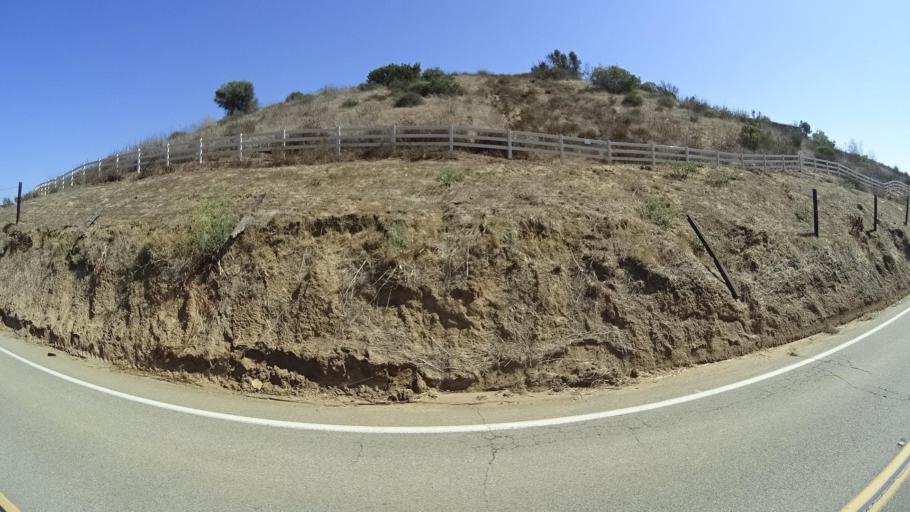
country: US
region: California
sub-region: San Diego County
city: Bonsall
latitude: 33.2985
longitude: -117.2109
